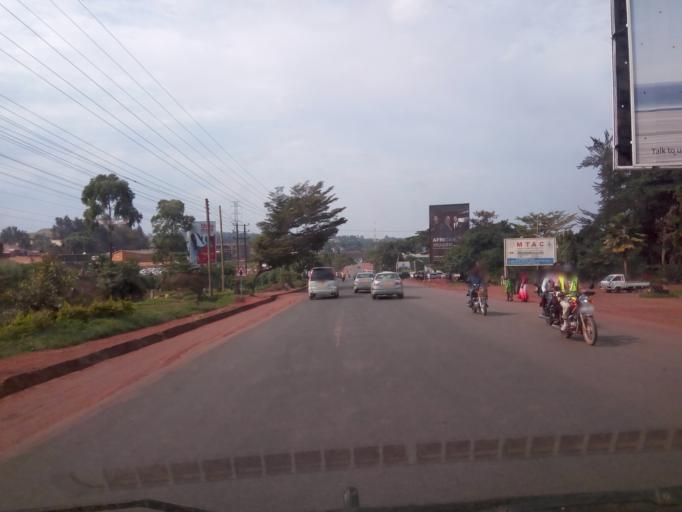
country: UG
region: Central Region
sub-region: Wakiso District
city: Kireka
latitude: 0.3328
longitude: 32.6169
